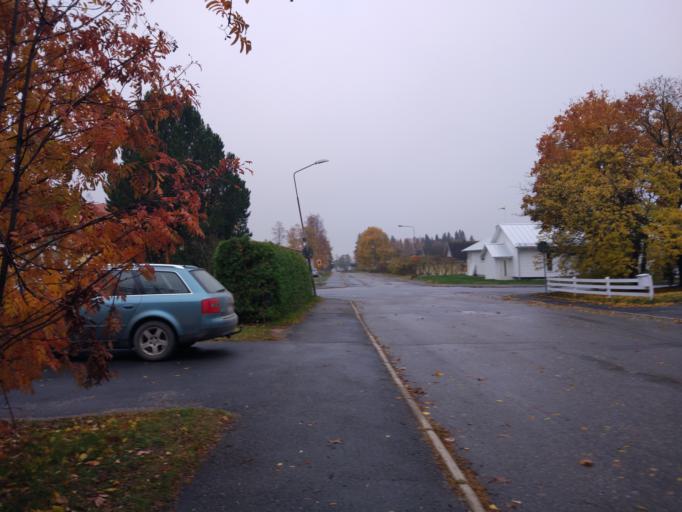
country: SE
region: Vaesterbotten
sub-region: Umea Kommun
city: Holmsund
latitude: 63.6988
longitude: 20.3679
